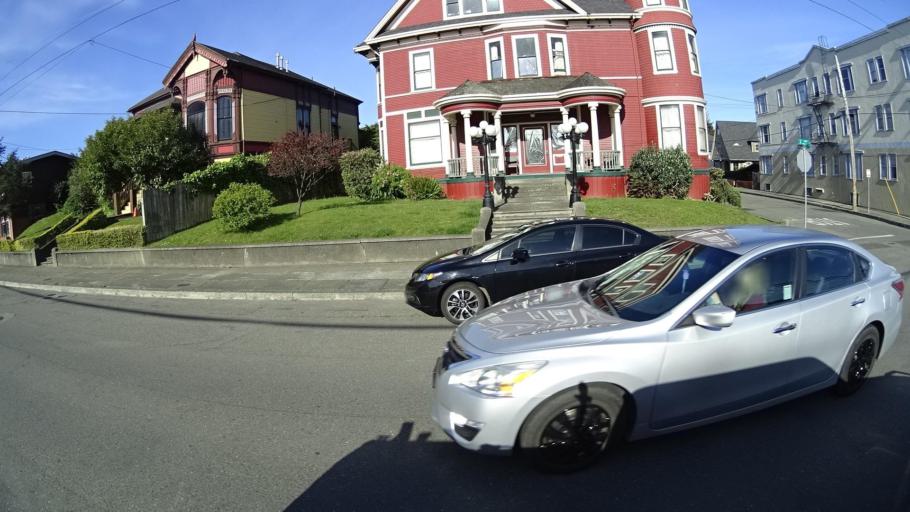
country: US
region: California
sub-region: Humboldt County
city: Eureka
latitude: 40.7953
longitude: -124.1655
